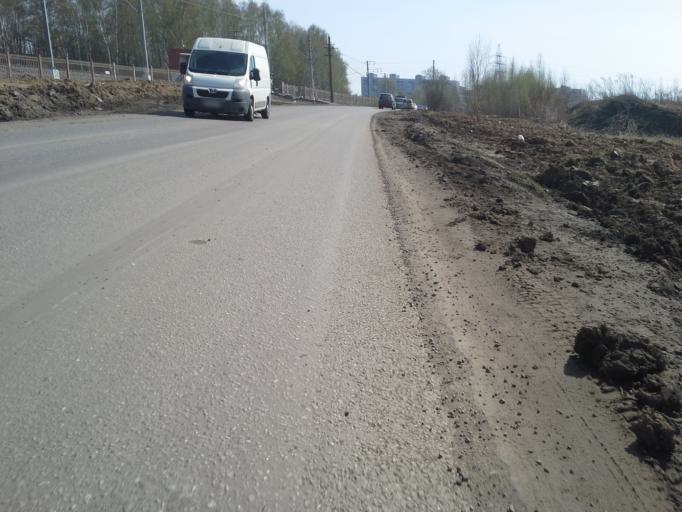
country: RU
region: Moskovskaya
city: Shcherbinka
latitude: 55.5220
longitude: 37.5339
